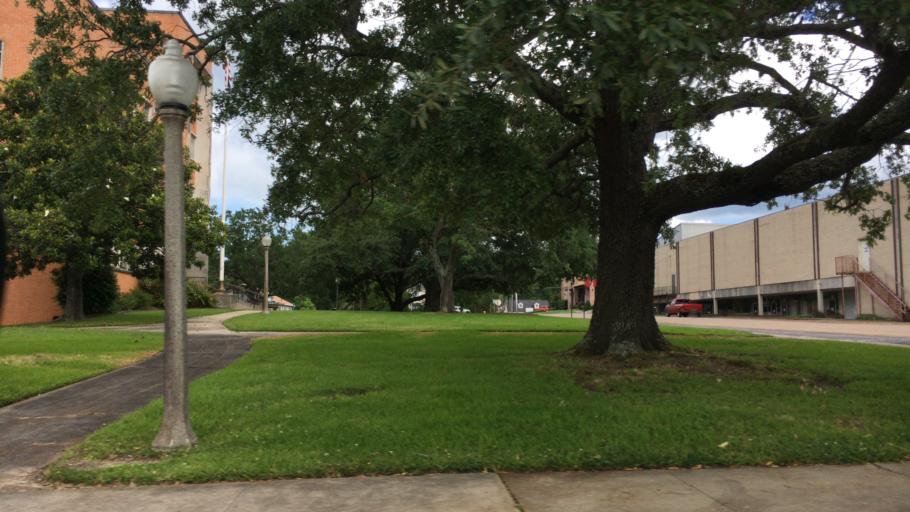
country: US
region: Louisiana
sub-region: Lincoln Parish
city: Ruston
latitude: 32.5270
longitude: -92.6394
